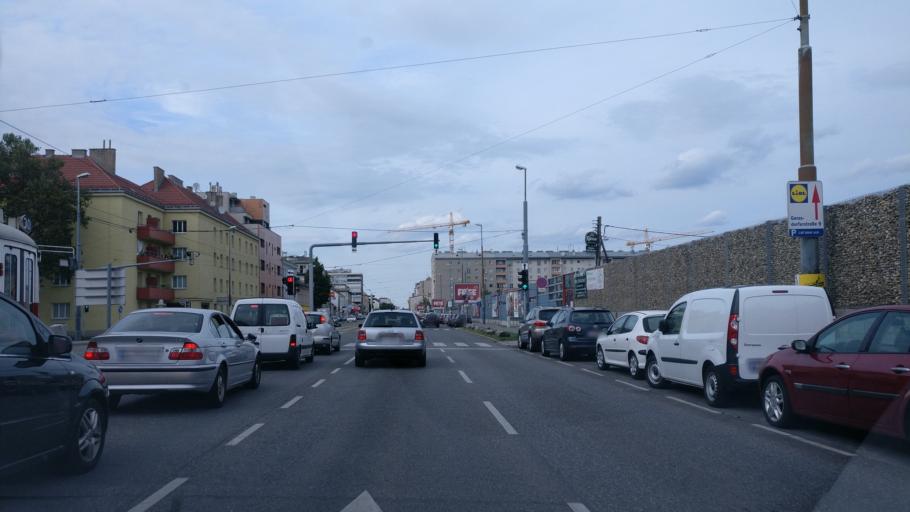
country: AT
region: Lower Austria
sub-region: Politischer Bezirk Korneuburg
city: Hagenbrunn
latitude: 48.2725
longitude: 16.4065
